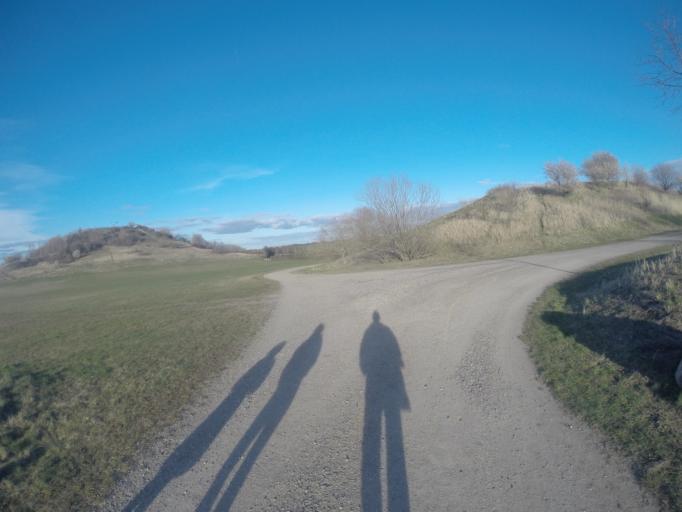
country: DK
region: Zealand
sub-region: Greve Kommune
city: Tune
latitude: 55.6239
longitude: 12.1712
